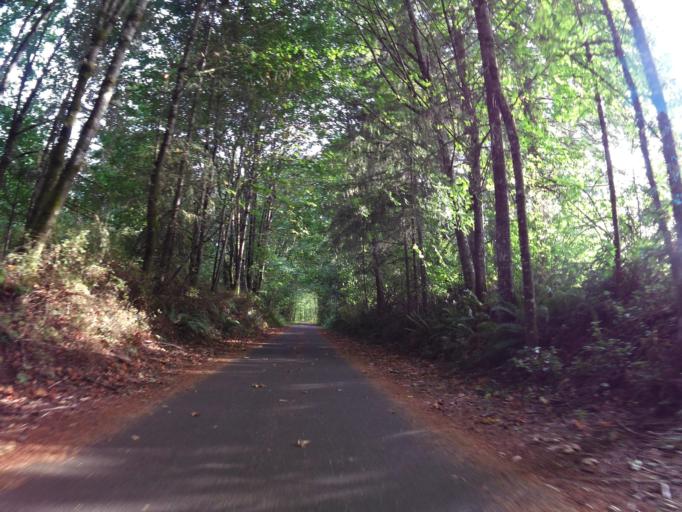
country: US
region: Washington
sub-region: Thurston County
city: Tenino
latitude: 46.9360
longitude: -122.8236
